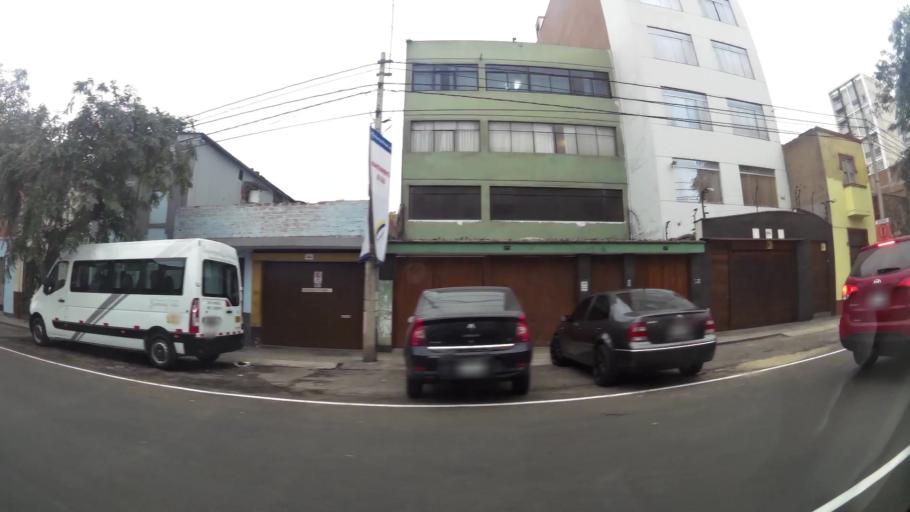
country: PE
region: Lima
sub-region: Lima
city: San Isidro
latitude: -12.0903
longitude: -77.0311
